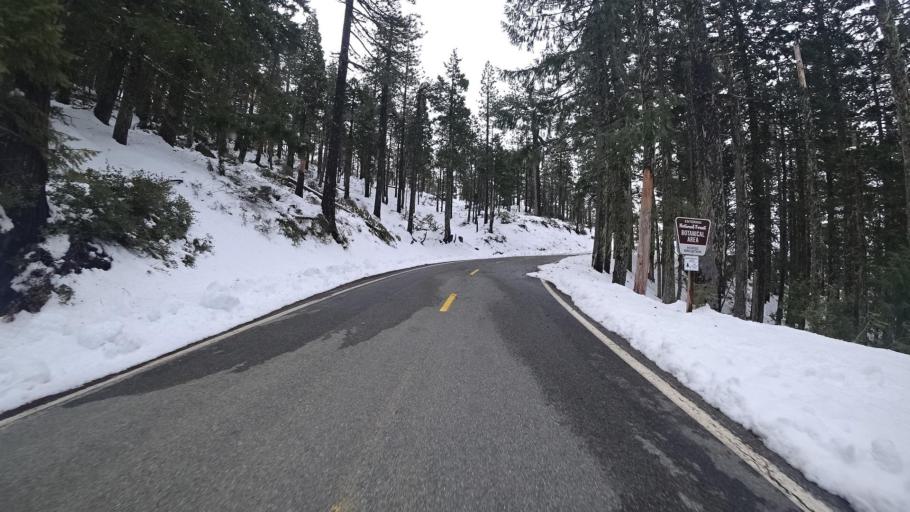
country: US
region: California
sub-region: Humboldt County
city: Willow Creek
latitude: 40.8668
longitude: -123.7367
